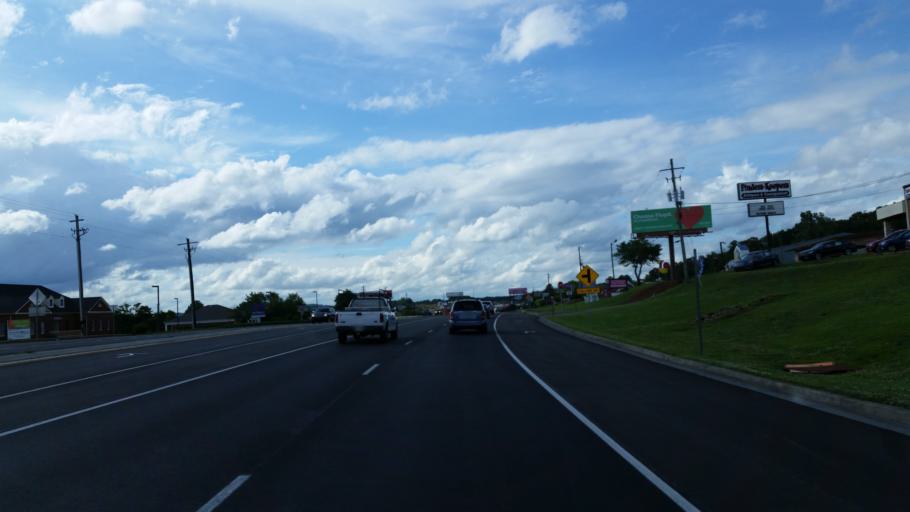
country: US
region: Georgia
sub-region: Bartow County
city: Cartersville
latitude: 34.1914
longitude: -84.7888
